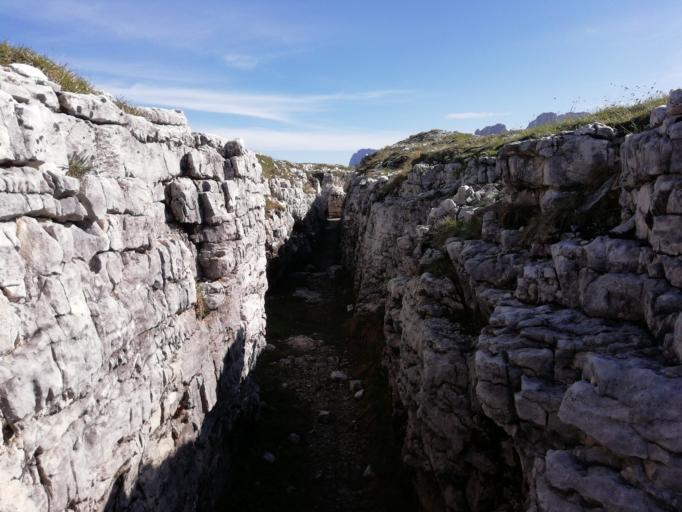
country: IT
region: Trentino-Alto Adige
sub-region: Bolzano
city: Dobbiaco
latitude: 46.6155
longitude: 12.2427
